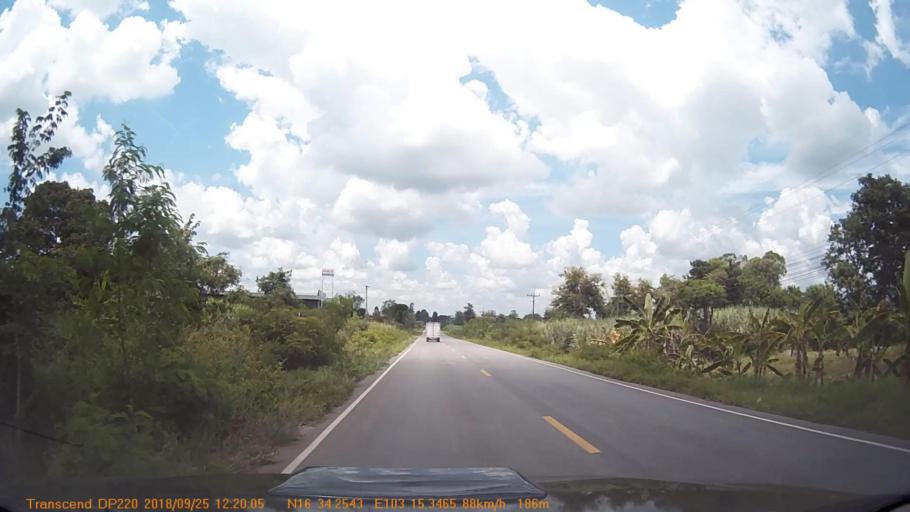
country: TH
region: Kalasin
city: Huai Mek
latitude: 16.5709
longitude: 103.2558
